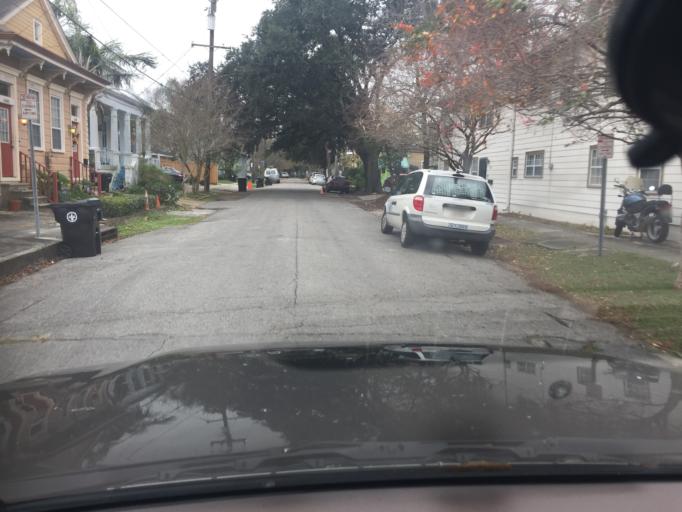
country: US
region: Louisiana
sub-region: Orleans Parish
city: New Orleans
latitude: 29.9821
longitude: -90.0758
